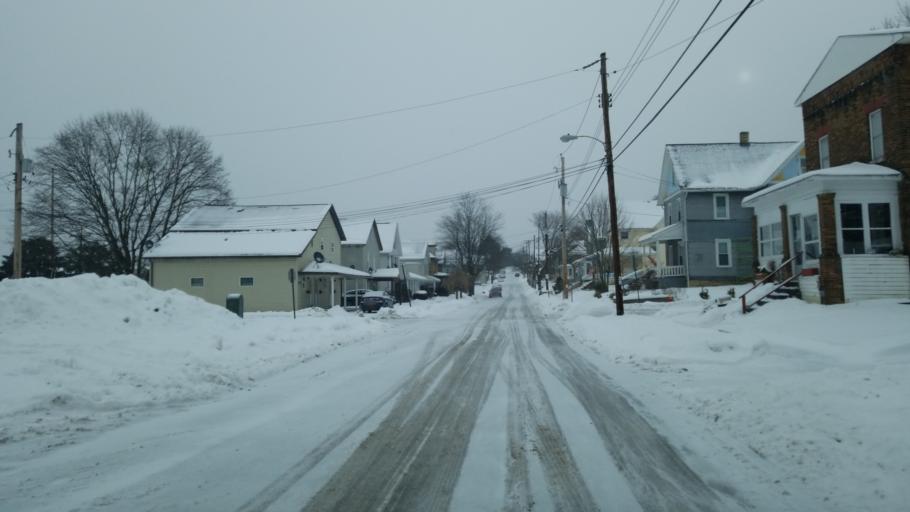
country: US
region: Pennsylvania
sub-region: Clearfield County
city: Clearfield
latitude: 41.0264
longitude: -78.4234
